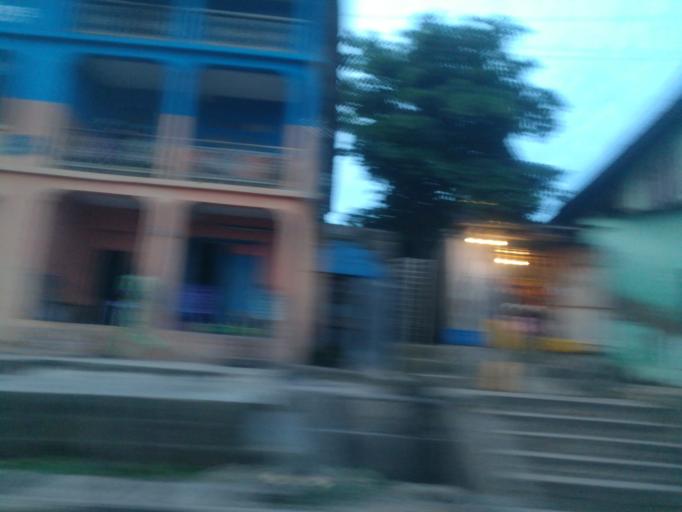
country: NG
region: Oyo
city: Ibadan
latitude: 7.3821
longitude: 3.8992
